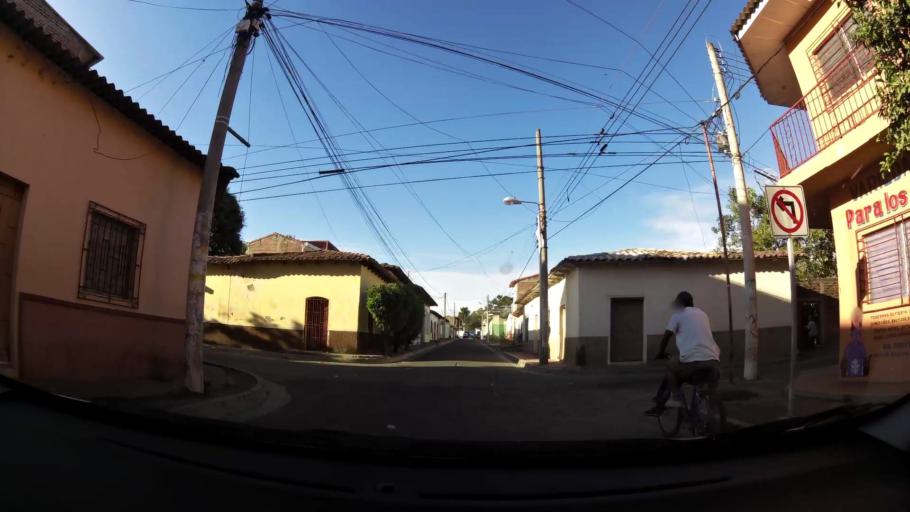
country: SV
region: Santa Ana
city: Metapan
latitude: 14.3345
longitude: -89.4475
